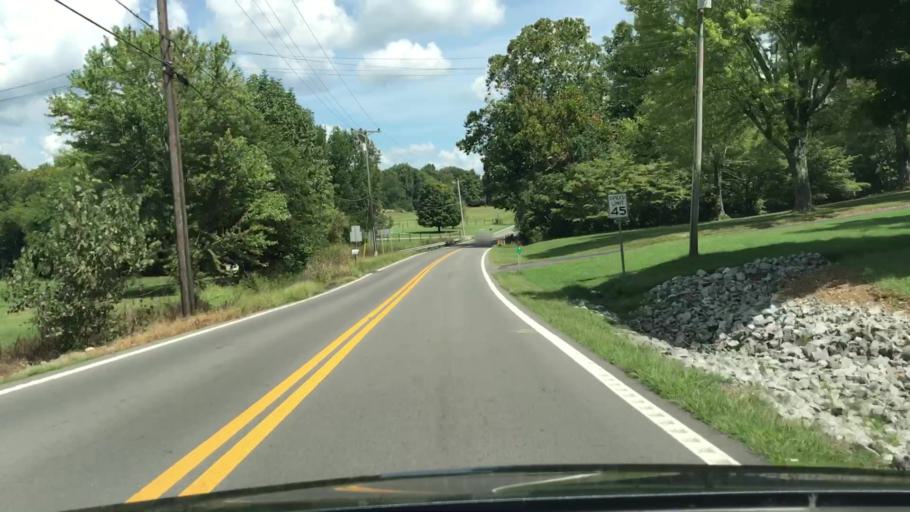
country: US
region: Tennessee
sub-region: Sumner County
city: White House
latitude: 36.4949
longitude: -86.5920
